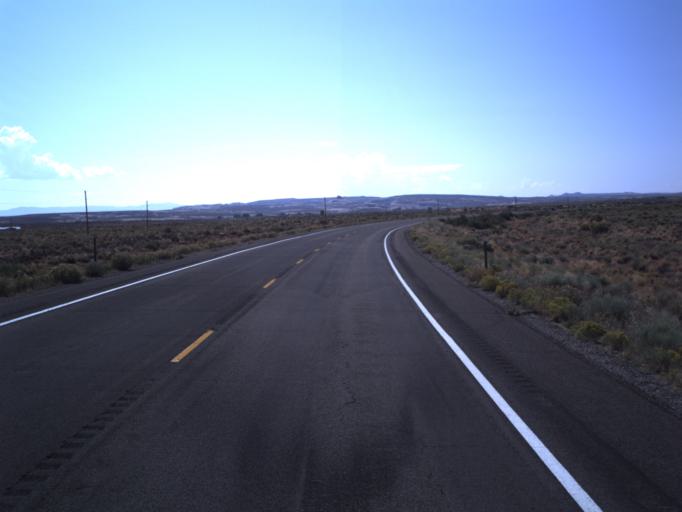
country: US
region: Utah
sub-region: San Juan County
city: Blanding
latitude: 37.1248
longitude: -109.5464
